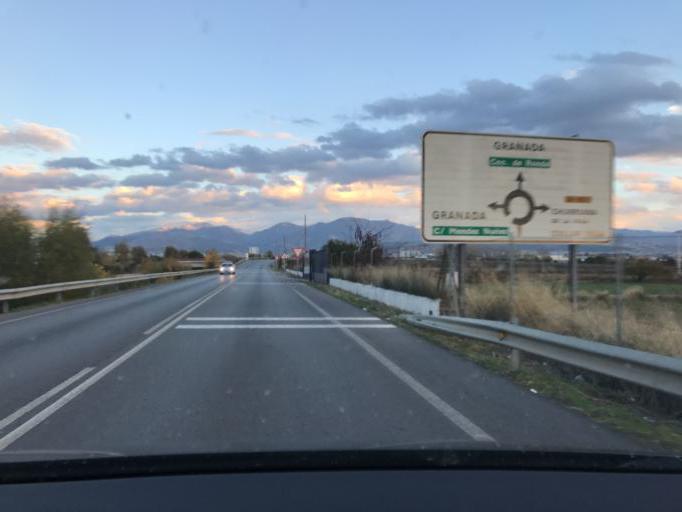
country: ES
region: Andalusia
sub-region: Provincia de Granada
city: Churriana de la Vega
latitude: 37.1640
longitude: -3.6304
